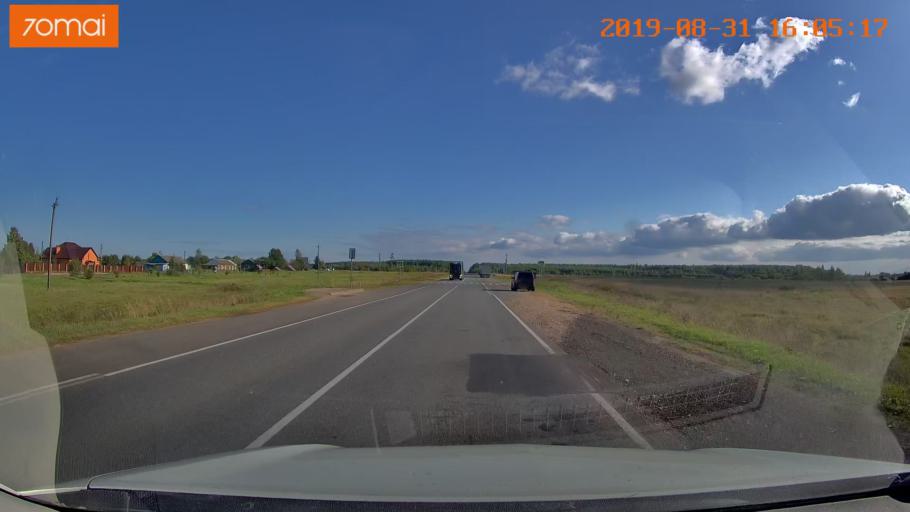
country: RU
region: Kaluga
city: Yukhnov
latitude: 54.6412
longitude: 35.3326
